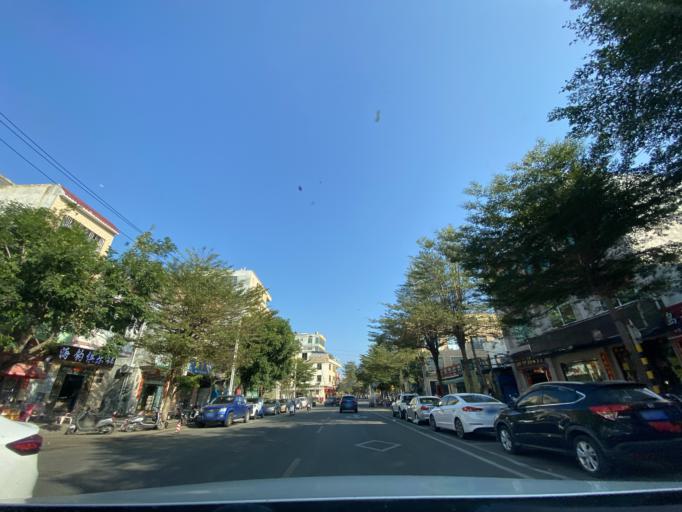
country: CN
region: Hainan
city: Xincun
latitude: 18.4132
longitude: 109.9646
